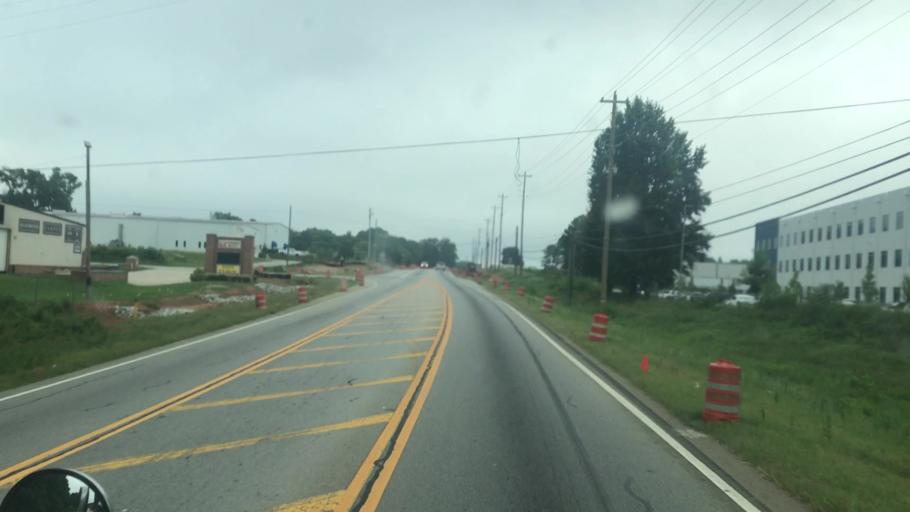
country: US
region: Georgia
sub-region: Henry County
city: McDonough
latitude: 33.3909
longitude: -84.1736
